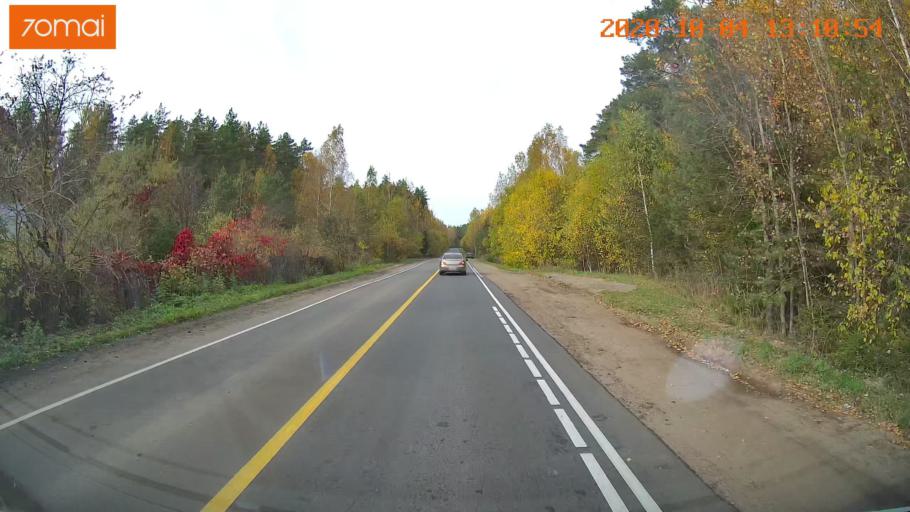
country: RU
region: Ivanovo
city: Bogorodskoye
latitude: 57.0731
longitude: 40.9498
